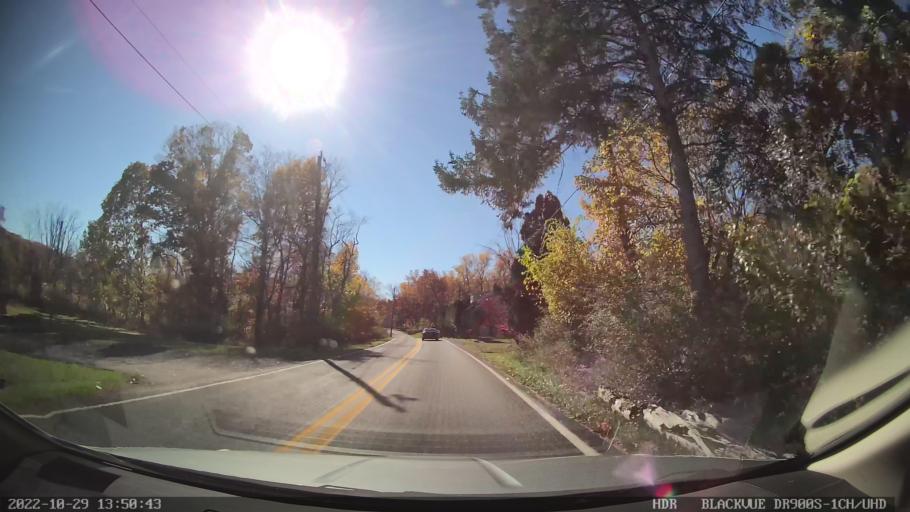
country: US
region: Pennsylvania
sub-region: Lehigh County
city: Emmaus
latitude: 40.5325
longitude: -75.4624
